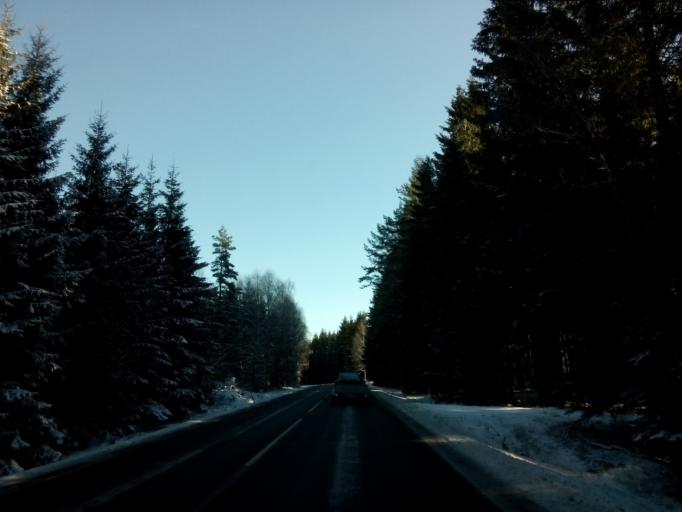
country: SE
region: Vaestra Goetaland
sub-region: Vargarda Kommun
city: Vargarda
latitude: 57.9842
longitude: 12.8705
